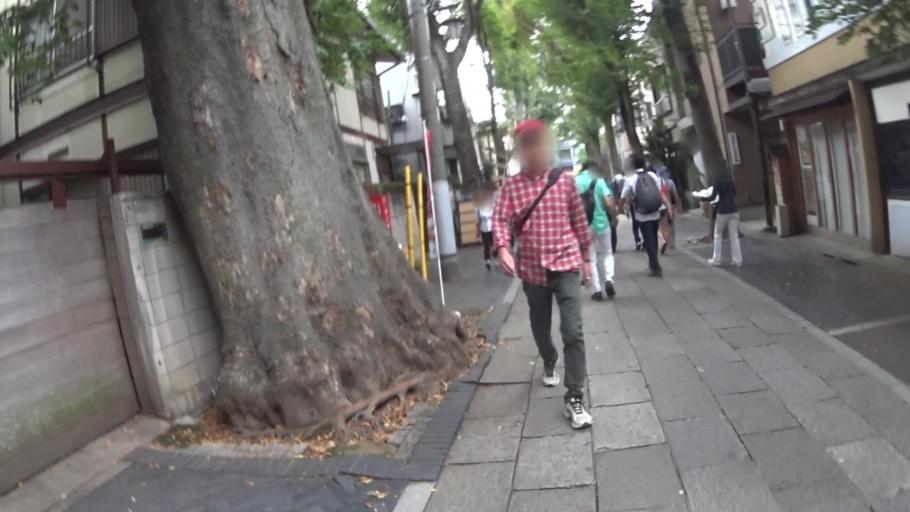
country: JP
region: Tokyo
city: Tokyo
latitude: 35.7212
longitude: 139.7146
